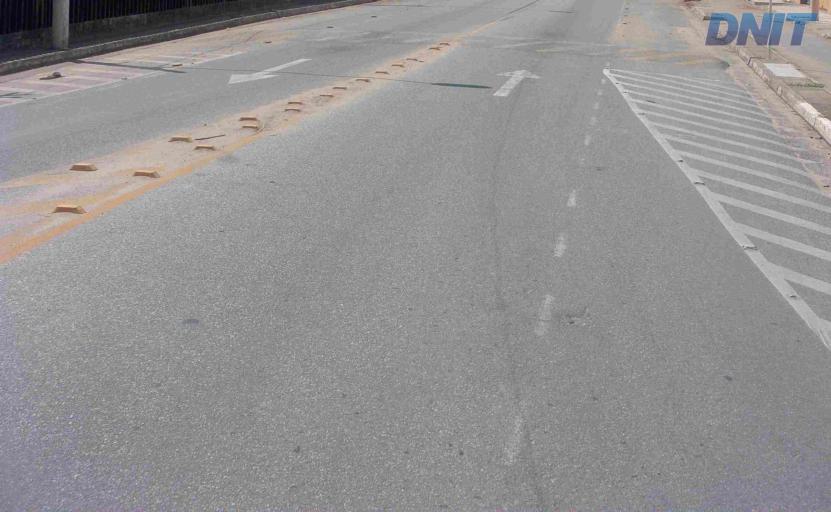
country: BR
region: Minas Gerais
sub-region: Governador Valadares
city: Governador Valadares
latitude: -18.9007
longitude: -41.9857
